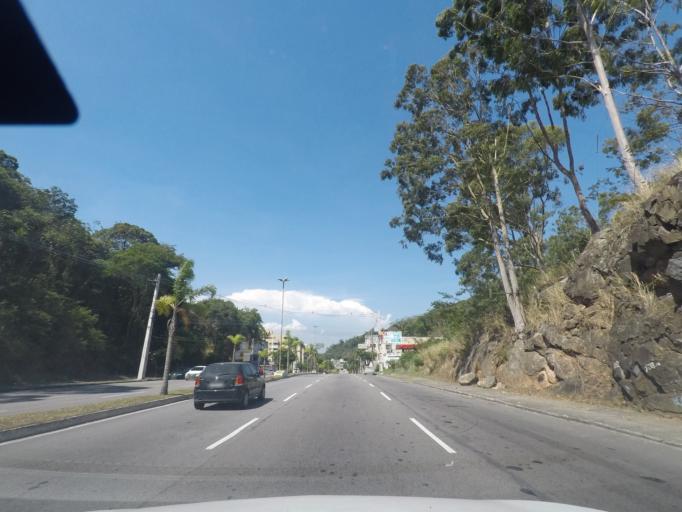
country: BR
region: Rio de Janeiro
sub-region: Niteroi
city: Niteroi
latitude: -22.9198
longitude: -43.0527
